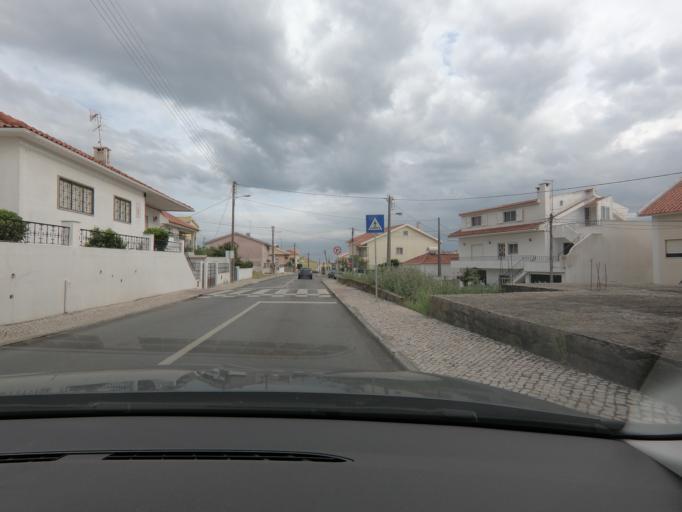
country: PT
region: Lisbon
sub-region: Cascais
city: Sao Domingos de Rana
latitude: 38.7154
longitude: -9.3328
